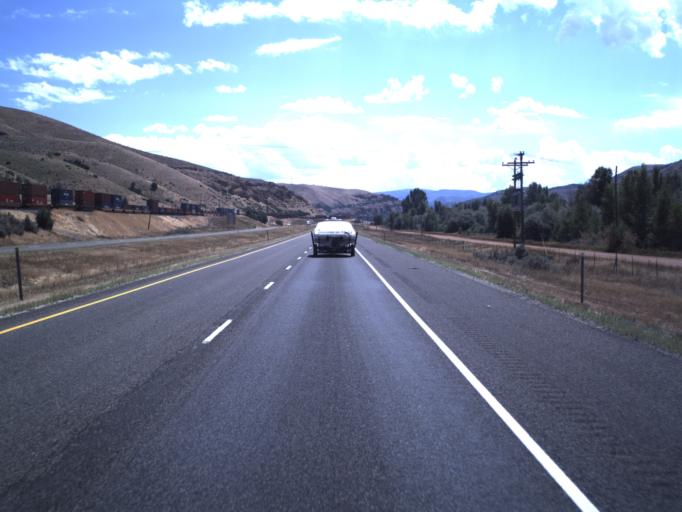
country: US
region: Utah
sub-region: Summit County
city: Coalville
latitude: 41.0068
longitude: -111.4772
